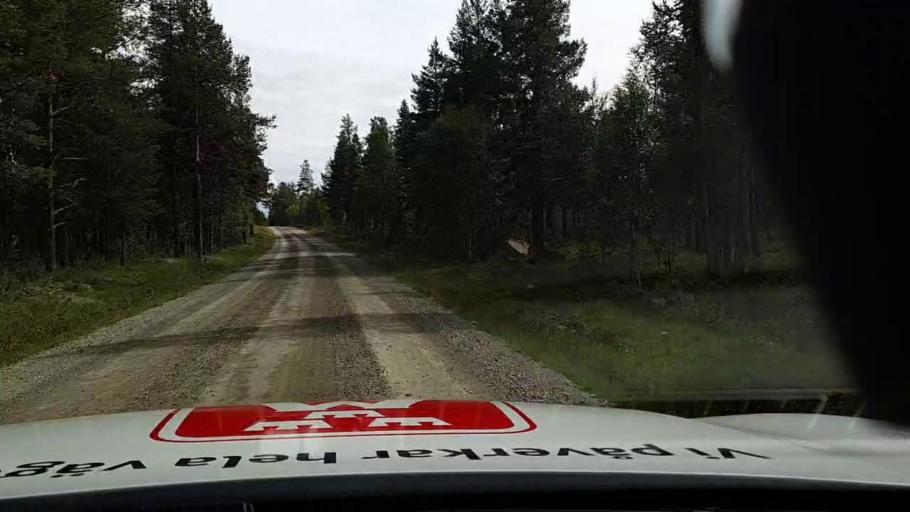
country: SE
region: Jaemtland
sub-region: Are Kommun
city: Jarpen
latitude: 62.5139
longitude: 13.4887
